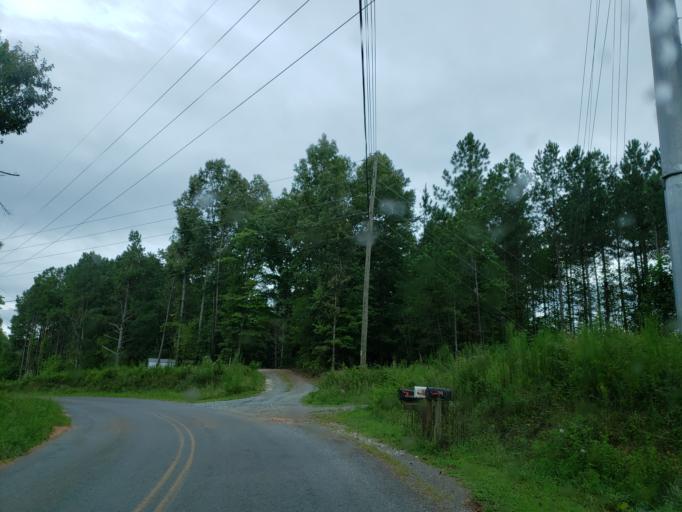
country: US
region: Georgia
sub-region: Gilmer County
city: Ellijay
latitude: 34.6154
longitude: -84.5697
